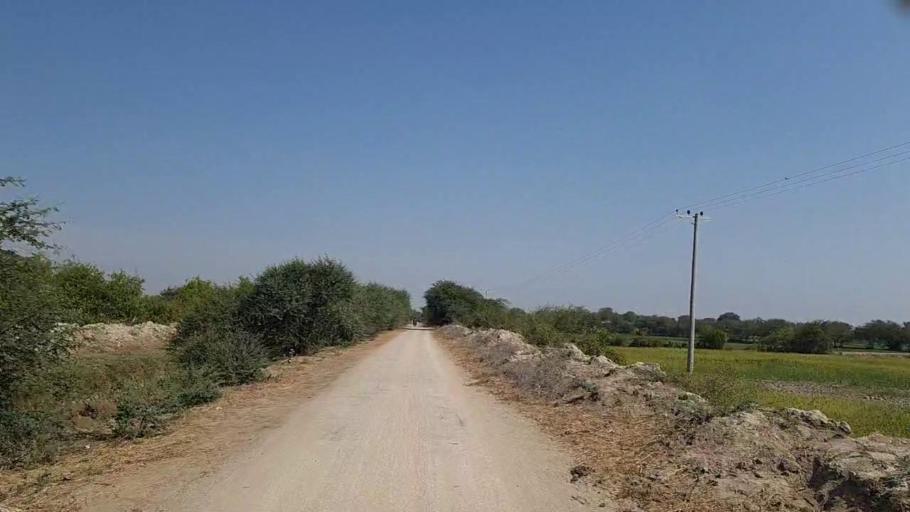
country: PK
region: Sindh
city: Mirpur Batoro
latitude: 24.6888
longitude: 68.2577
